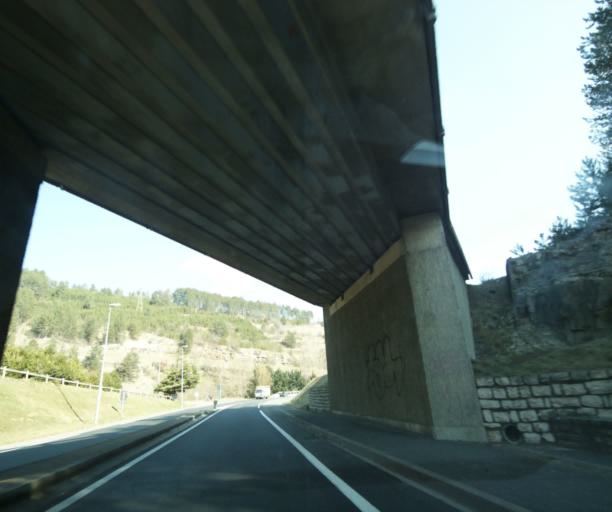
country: FR
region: Languedoc-Roussillon
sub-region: Departement de la Lozere
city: Mende
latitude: 44.5261
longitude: 3.5128
